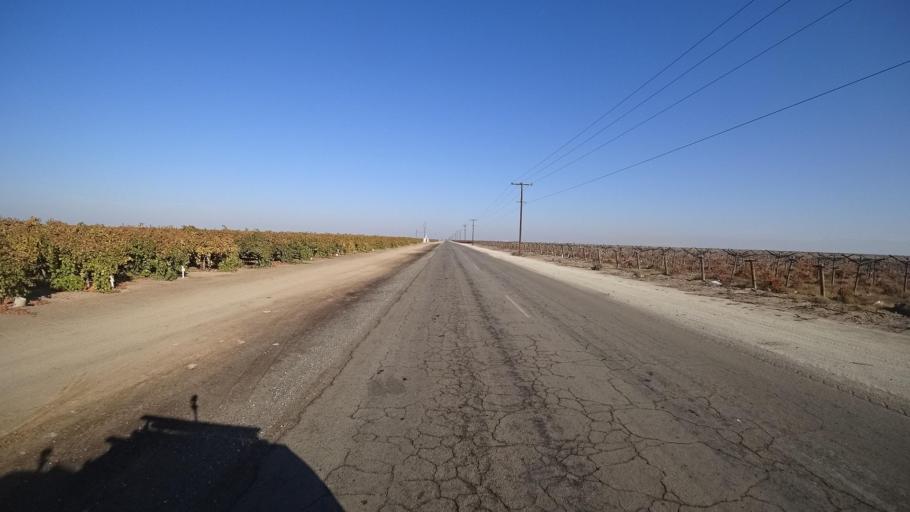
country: US
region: California
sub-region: Tulare County
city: Richgrove
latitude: 35.7525
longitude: -119.1696
